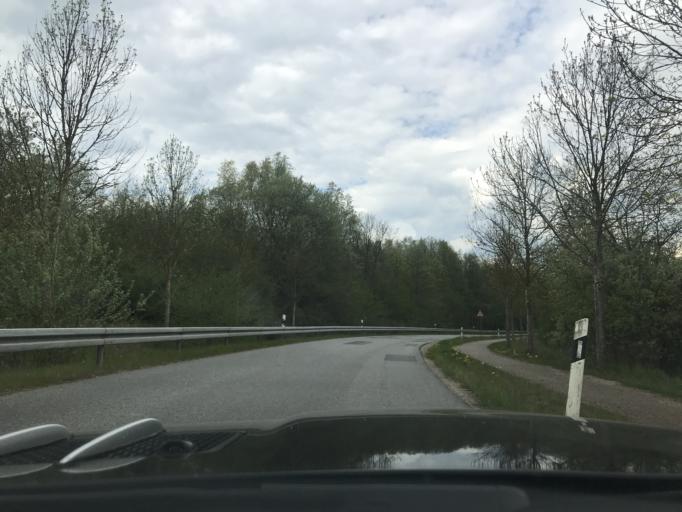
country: DE
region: Schleswig-Holstein
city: Gross Gronau
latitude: 53.7726
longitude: 10.7699
